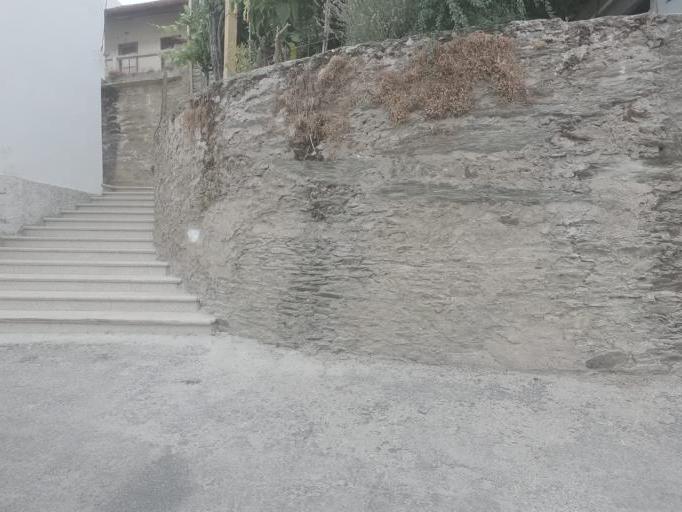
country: PT
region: Vila Real
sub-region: Sabrosa
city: Vilela
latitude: 41.1999
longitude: -7.5335
